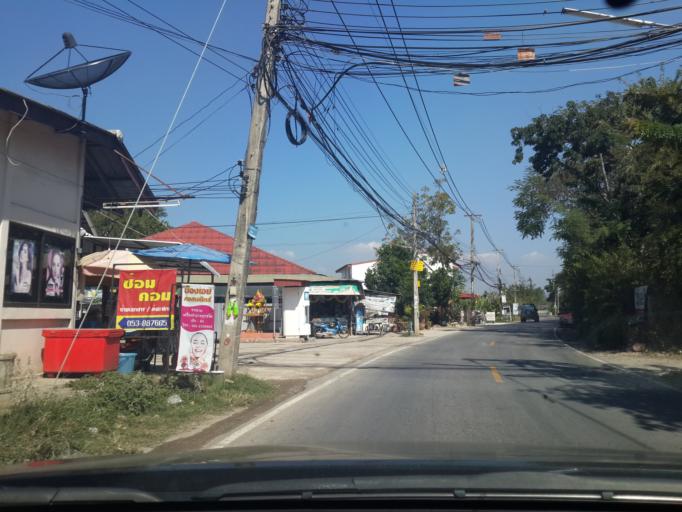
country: TH
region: Chiang Mai
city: San Sai
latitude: 18.8581
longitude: 99.0885
